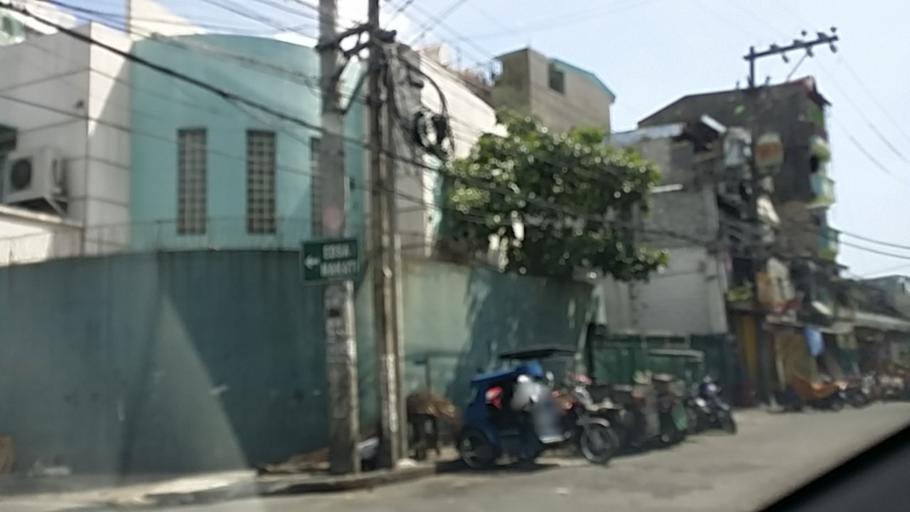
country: PH
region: Metro Manila
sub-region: Mandaluyong
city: Mandaluyong City
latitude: 14.5777
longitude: 121.0487
